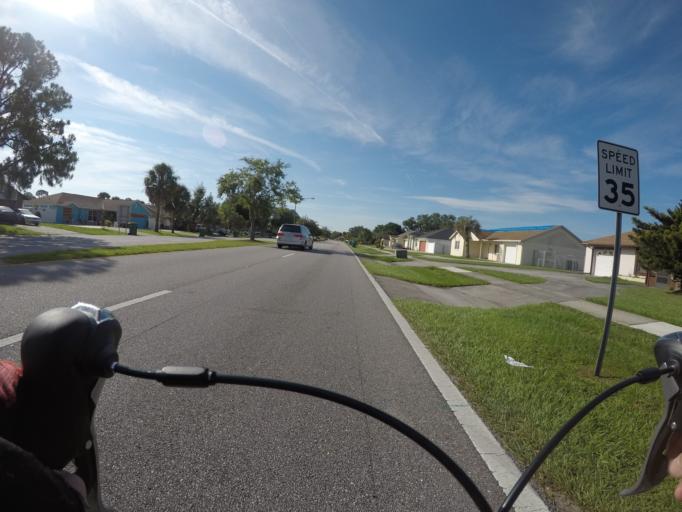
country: US
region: Florida
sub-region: Osceola County
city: Buenaventura Lakes
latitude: 28.3282
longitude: -81.3508
